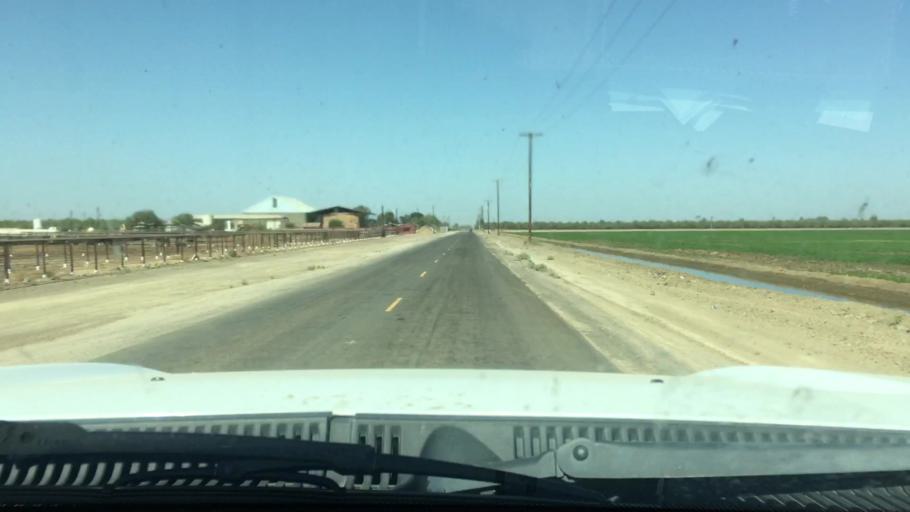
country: US
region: California
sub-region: Kern County
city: Shafter
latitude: 35.4669
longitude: -119.3143
